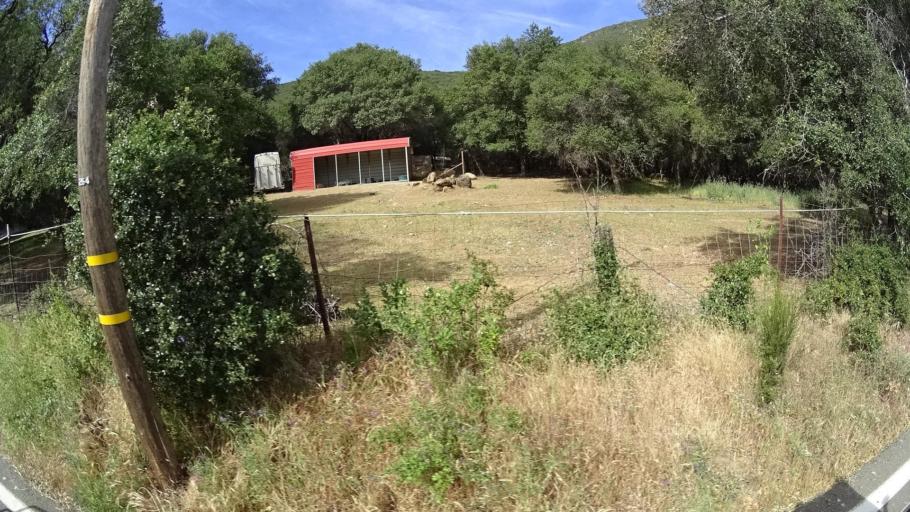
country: US
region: California
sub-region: Lake County
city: Soda Bay
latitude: 38.9699
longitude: -122.7434
